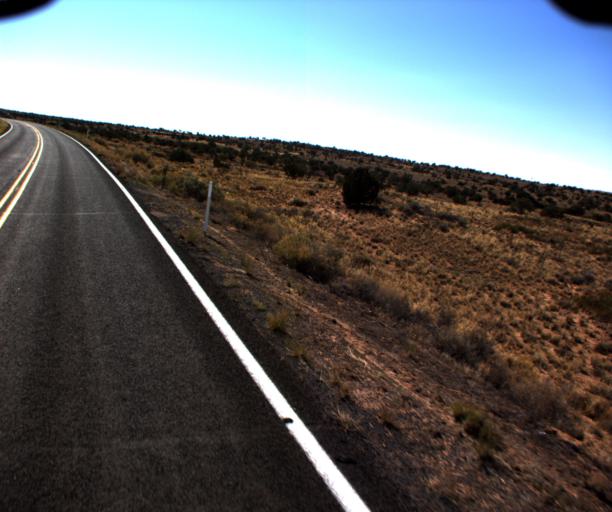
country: US
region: Arizona
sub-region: Coconino County
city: Tuba City
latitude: 35.9597
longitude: -110.8519
